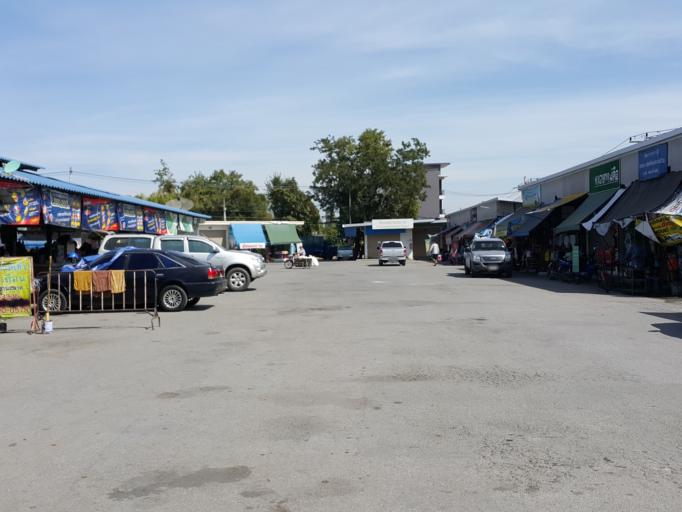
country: TH
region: Chiang Mai
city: San Kamphaeng
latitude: 18.7941
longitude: 99.1047
